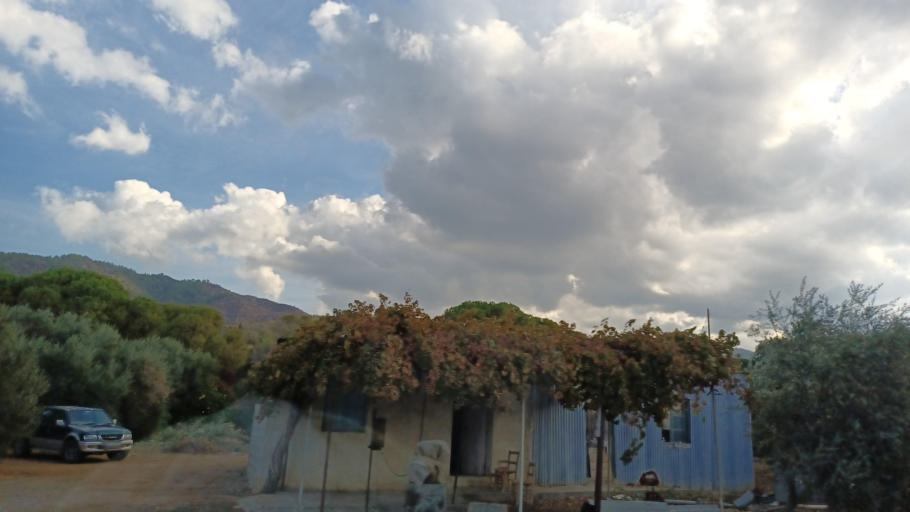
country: CY
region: Pafos
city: Polis
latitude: 35.1325
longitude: 32.5196
